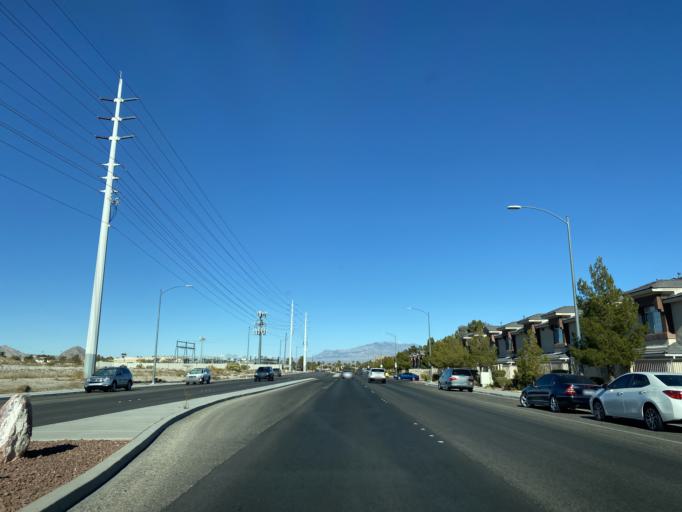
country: US
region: Nevada
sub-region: Clark County
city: Spring Valley
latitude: 36.1840
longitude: -115.2784
